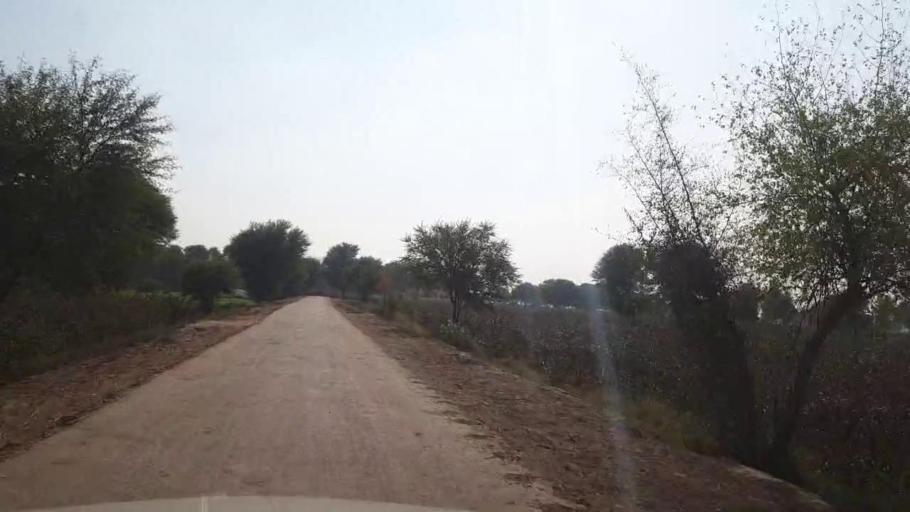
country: PK
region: Sindh
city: Bhan
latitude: 26.5324
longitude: 67.7632
